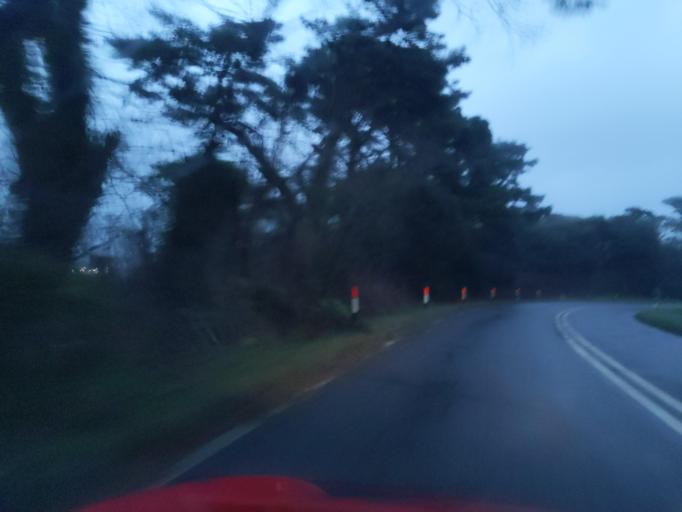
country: GB
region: England
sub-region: Cornwall
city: Torpoint
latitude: 50.3832
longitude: -4.2117
